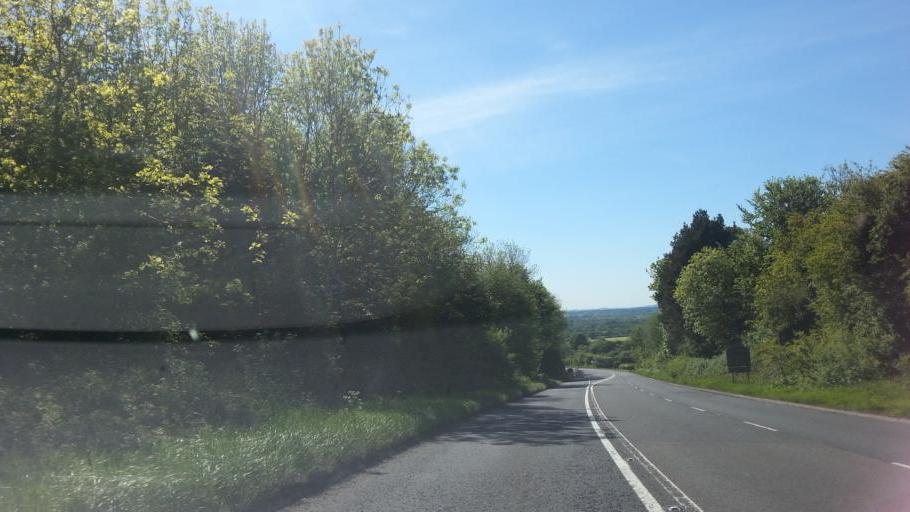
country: GB
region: England
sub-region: Dorset
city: Shaftesbury
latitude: 51.0085
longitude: -2.2022
